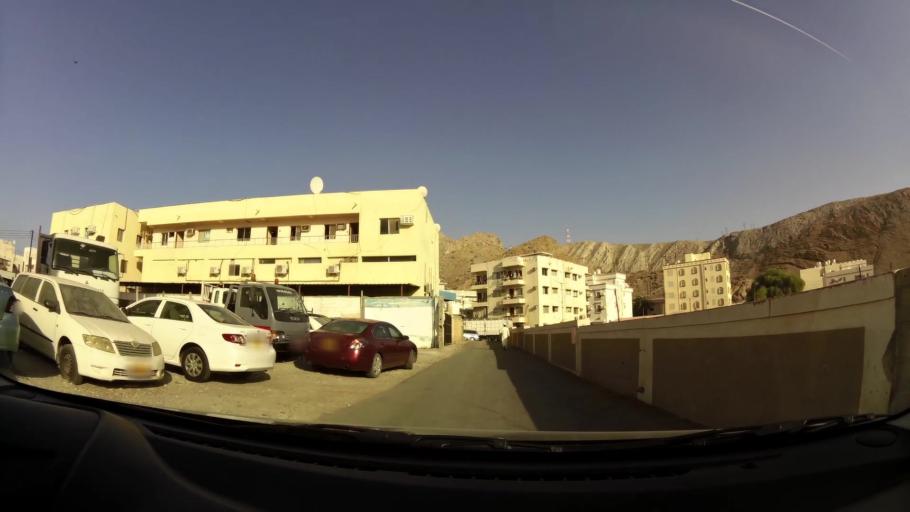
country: OM
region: Muhafazat Masqat
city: Muscat
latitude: 23.5865
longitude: 58.5518
